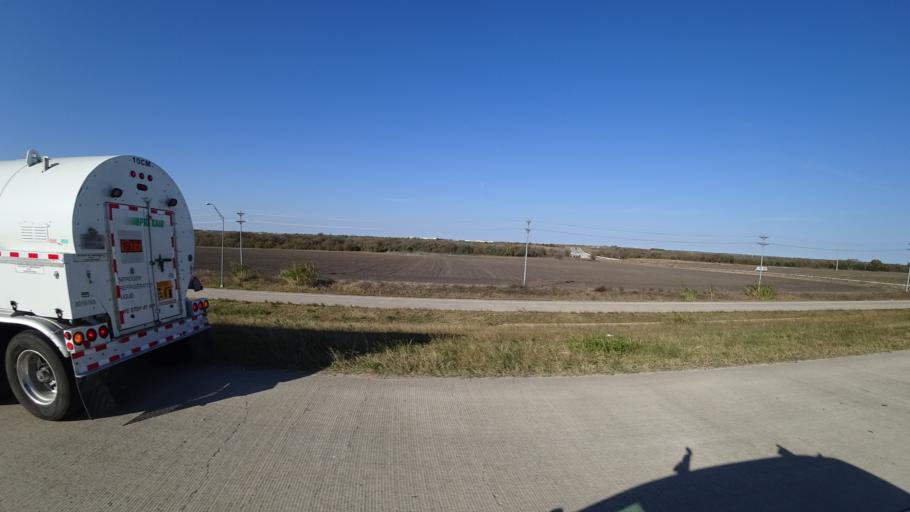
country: US
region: Texas
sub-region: Travis County
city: Manor
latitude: 30.3684
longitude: -97.5840
